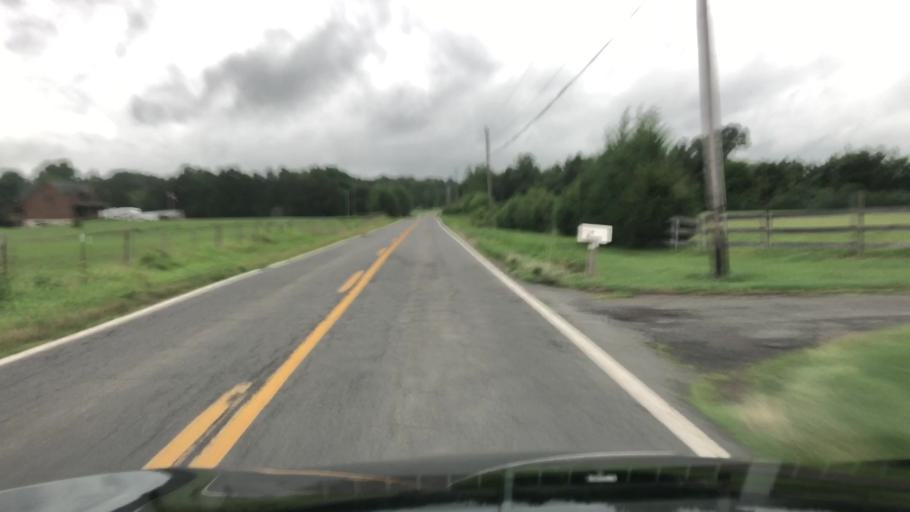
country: US
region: Virginia
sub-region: Prince William County
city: Nokesville
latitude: 38.5905
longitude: -77.6039
